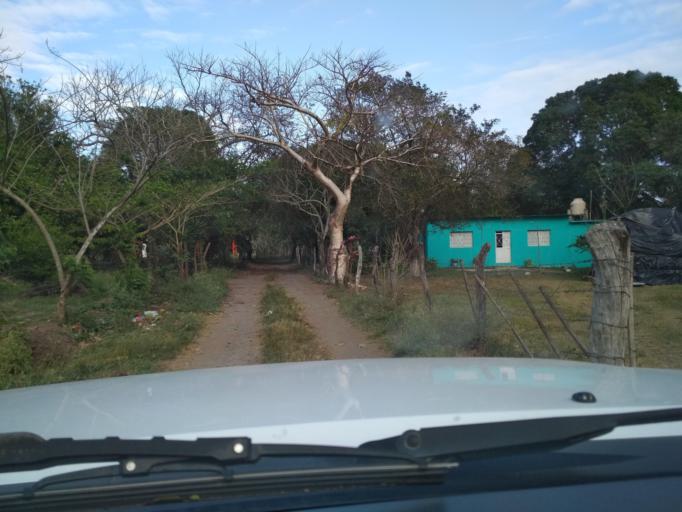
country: MX
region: Veracruz
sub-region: Veracruz
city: Delfino Victoria (Santa Fe)
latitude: 19.1504
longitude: -96.2977
